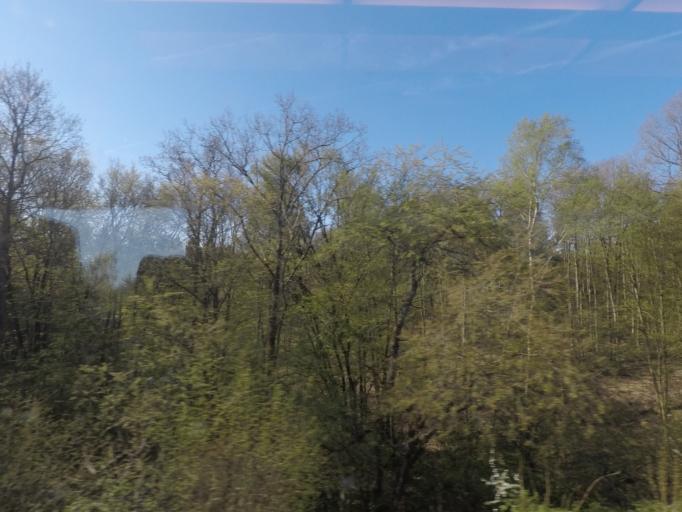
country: BE
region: Wallonia
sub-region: Province du Luxembourg
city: Marche-en-Famenne
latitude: 50.2490
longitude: 5.2618
